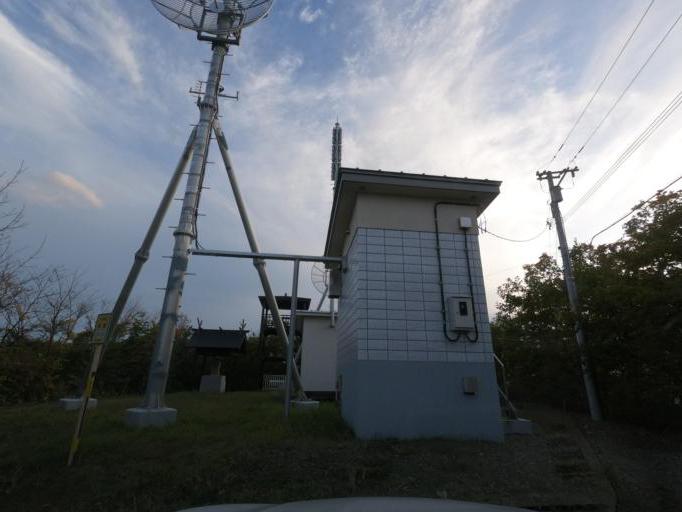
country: JP
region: Hokkaido
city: Obihiro
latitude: 42.5829
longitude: 143.3139
